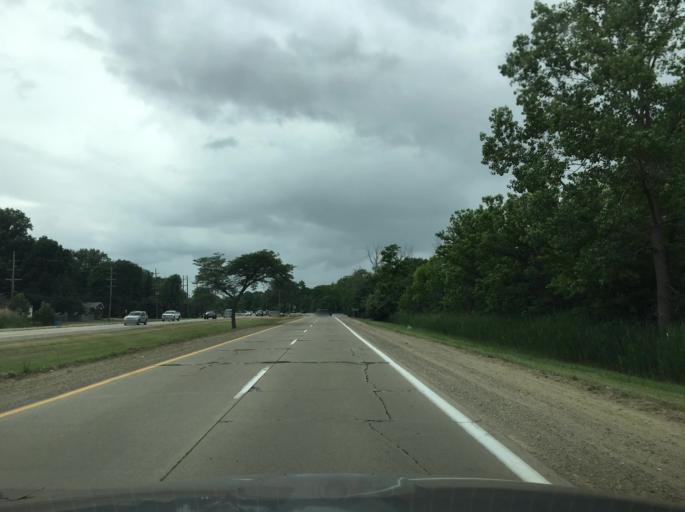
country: US
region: Michigan
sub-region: Macomb County
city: Mount Clemens
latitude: 42.5739
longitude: -82.8418
